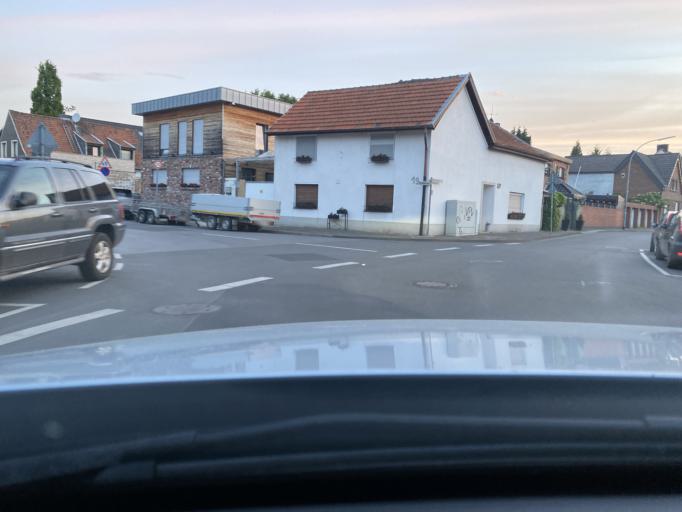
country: DE
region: North Rhine-Westphalia
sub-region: Regierungsbezirk Dusseldorf
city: Grevenbroich
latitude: 51.0976
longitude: 6.5754
